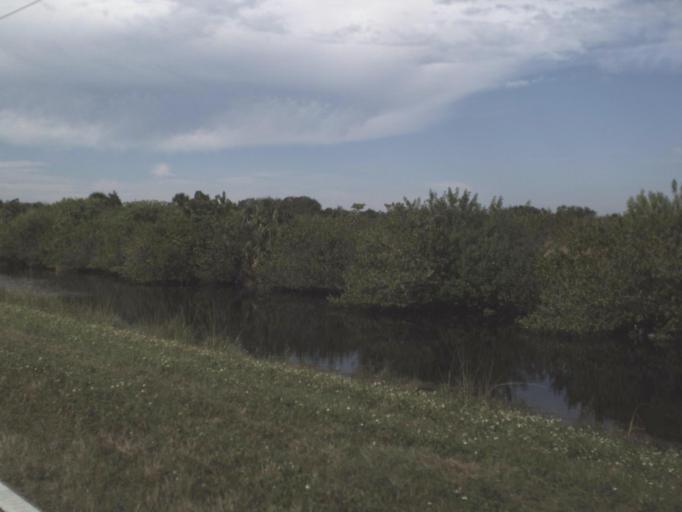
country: US
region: Florida
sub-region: Brevard County
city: Merritt Island
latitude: 28.5264
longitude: -80.7098
